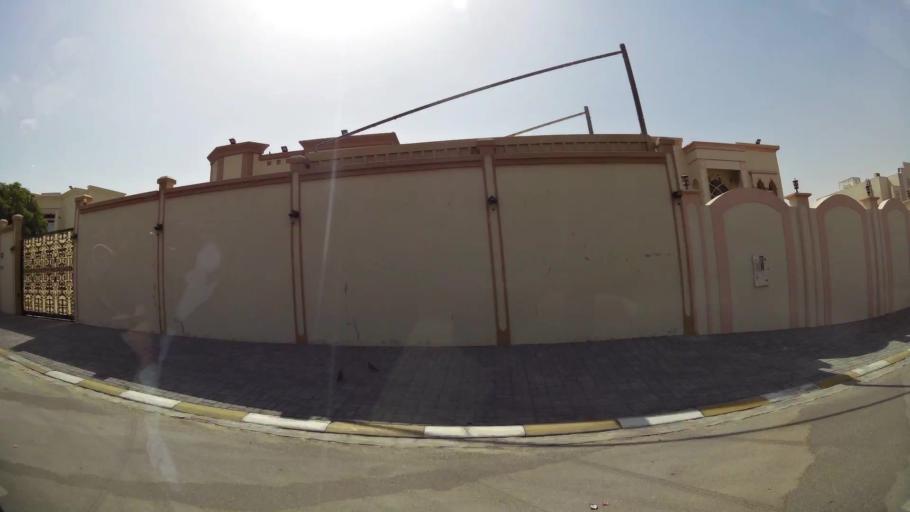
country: AE
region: Ash Shariqah
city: Sharjah
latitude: 25.2019
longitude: 55.4079
